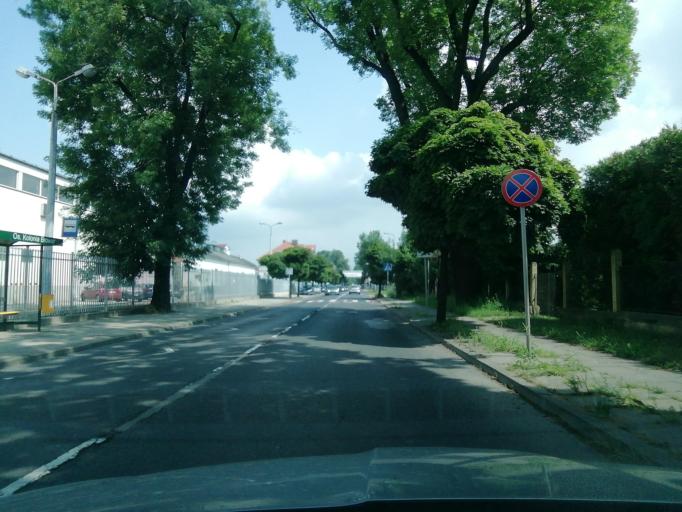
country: PL
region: Silesian Voivodeship
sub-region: Powiat zywiecki
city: Wieprz
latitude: 49.6608
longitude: 19.1736
